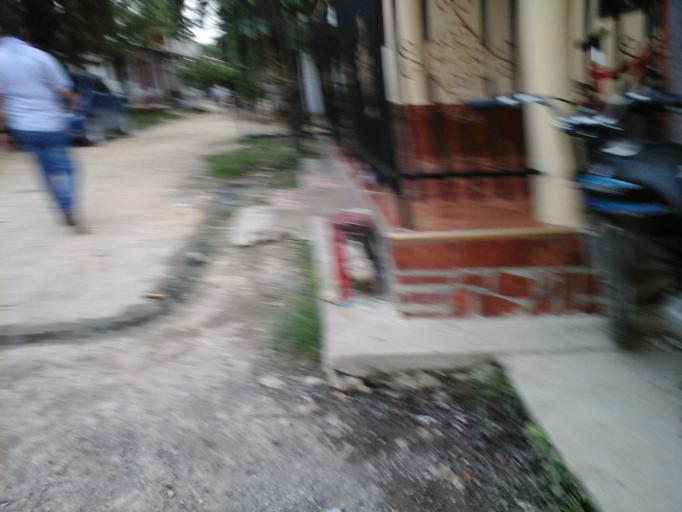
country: CO
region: Bolivar
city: San Pablo
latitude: 10.1422
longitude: -75.2734
